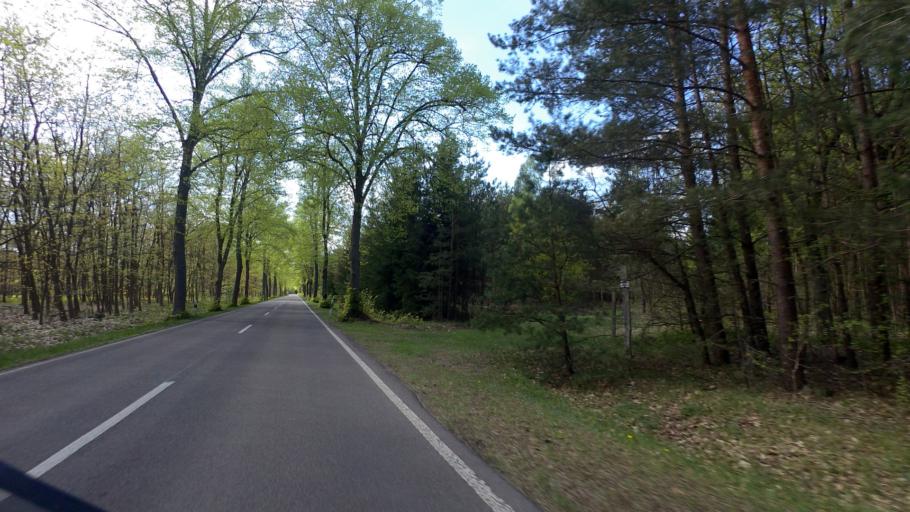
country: DE
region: Brandenburg
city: Friedrichswalde
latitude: 53.0020
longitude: 13.5879
